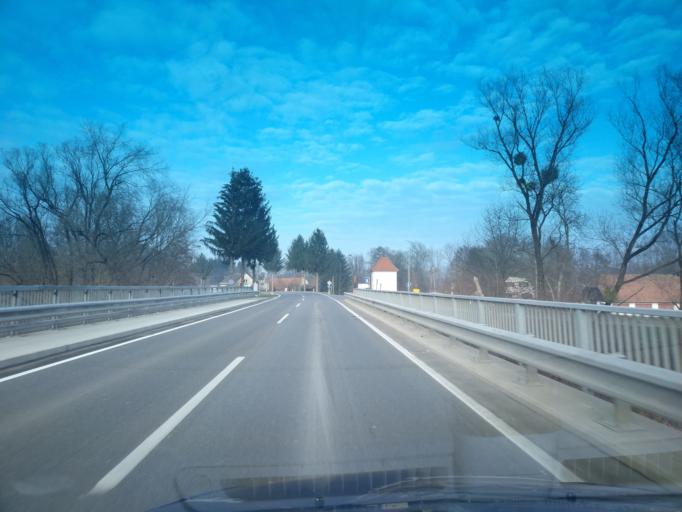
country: AT
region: Styria
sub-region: Politischer Bezirk Leibnitz
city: Spielfeld
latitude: 46.7100
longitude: 15.6341
